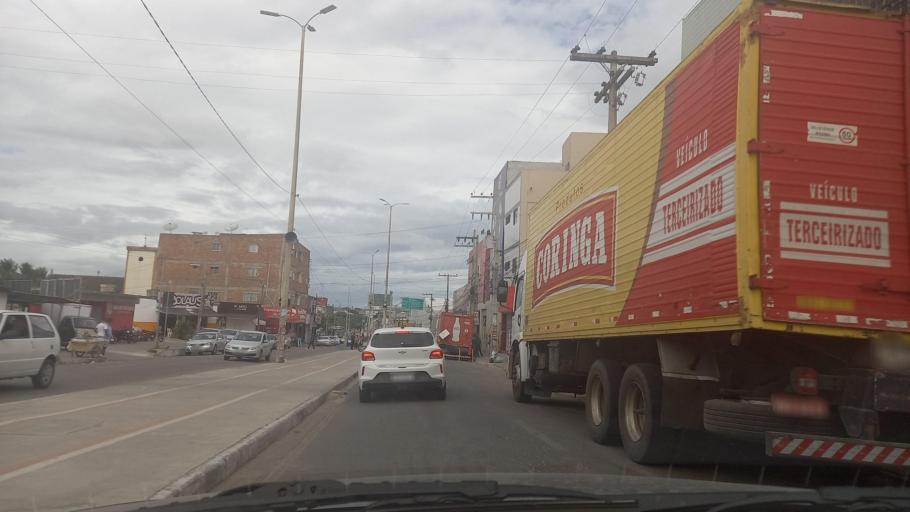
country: BR
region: Pernambuco
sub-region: Caruaru
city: Caruaru
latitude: -8.2750
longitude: -35.9887
